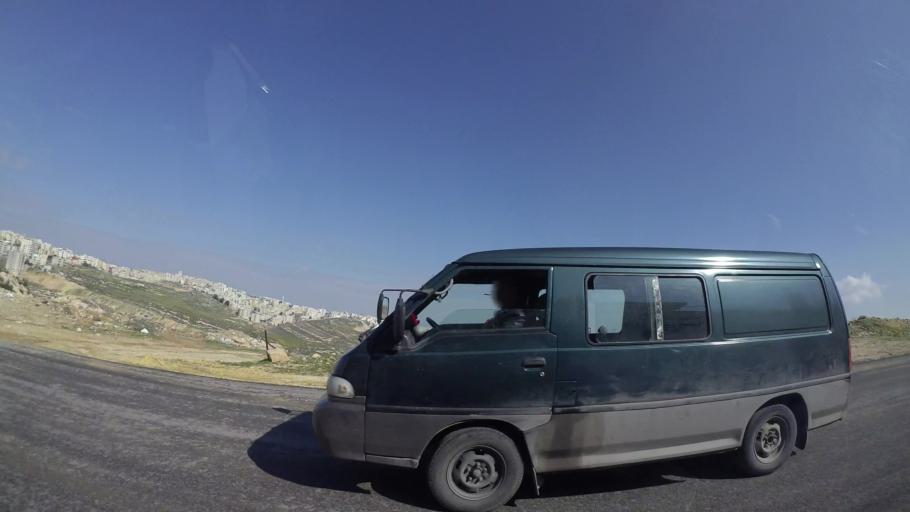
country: JO
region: Amman
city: Al Jubayhah
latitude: 31.9994
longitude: 35.8981
